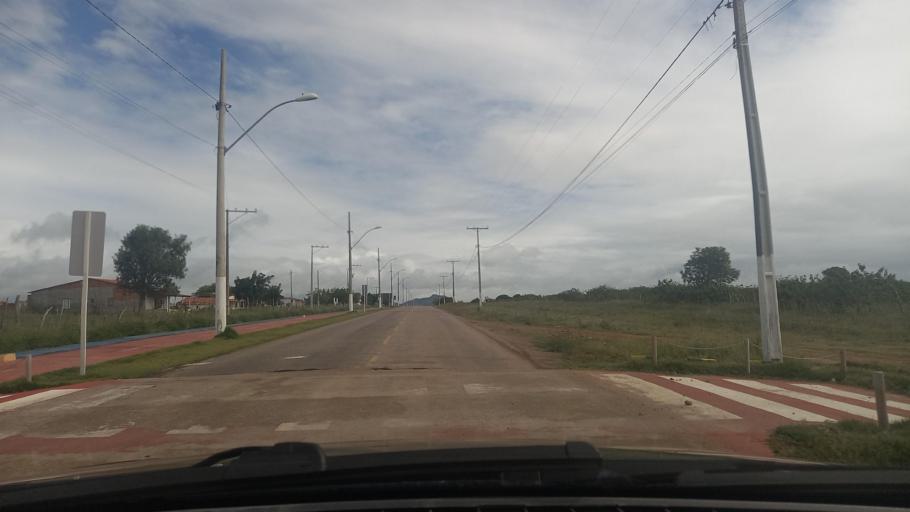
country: BR
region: Bahia
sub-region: Paulo Afonso
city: Paulo Afonso
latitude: -9.3511
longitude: -38.2625
